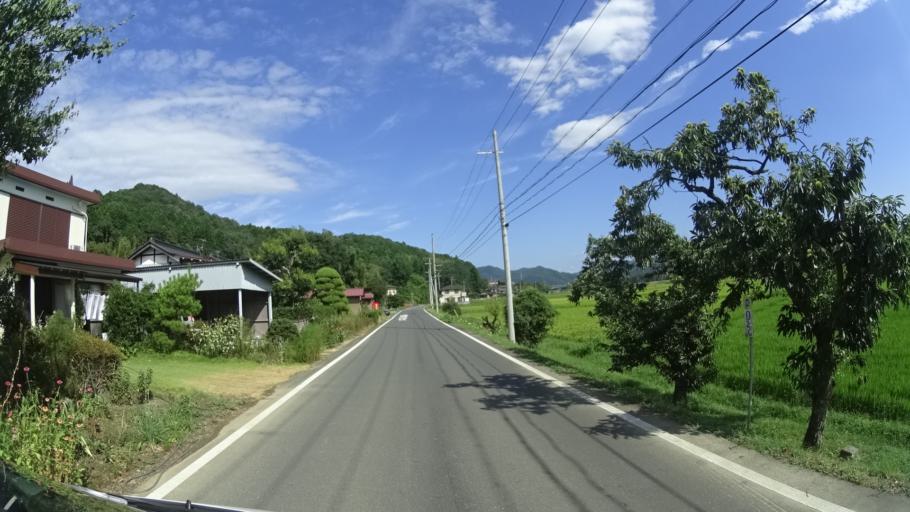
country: JP
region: Kyoto
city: Ayabe
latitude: 35.3176
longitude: 135.1864
